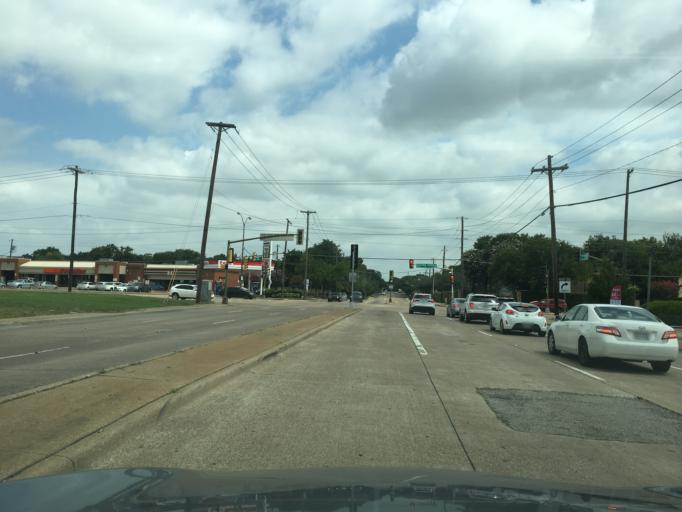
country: US
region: Texas
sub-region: Dallas County
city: Addison
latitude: 32.9388
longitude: -96.8139
